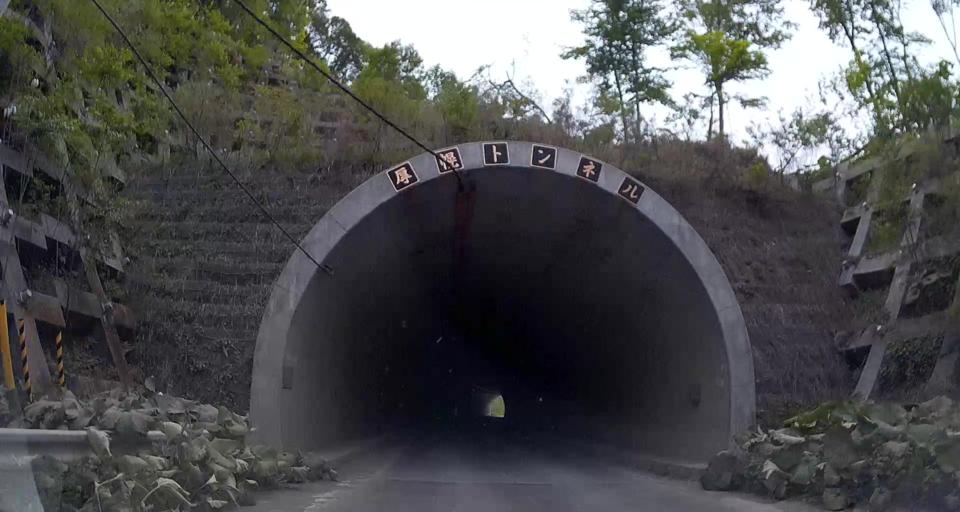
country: JP
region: Hokkaido
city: Chitose
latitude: 42.7648
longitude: 141.9969
